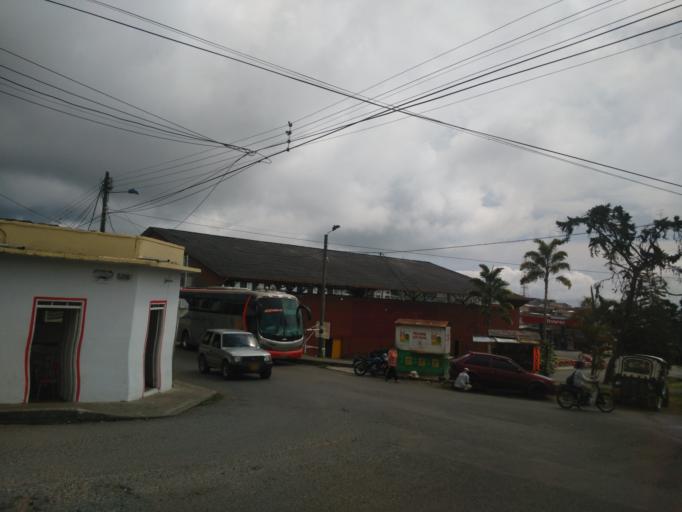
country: CO
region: Valle del Cauca
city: Sevilla
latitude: 4.2671
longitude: -75.9314
